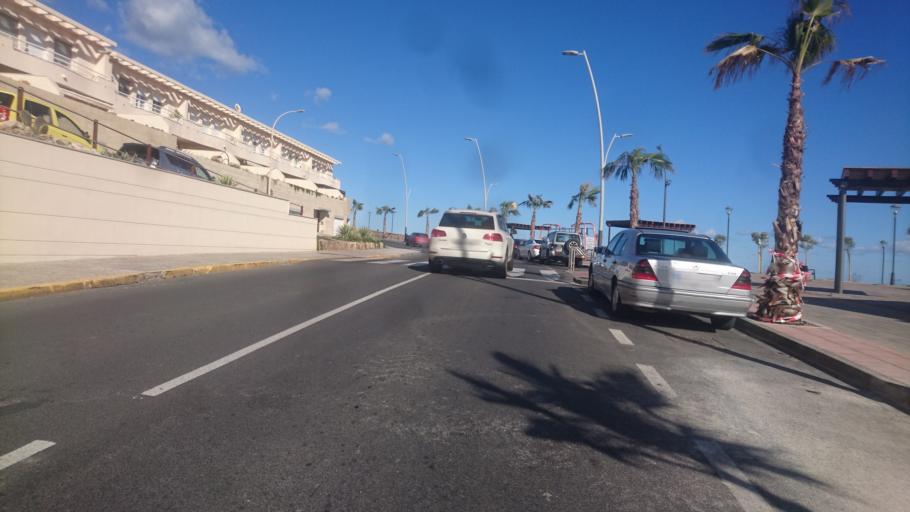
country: ES
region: Melilla
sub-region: Melilla
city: Melilla
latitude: 35.2954
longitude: -2.9360
